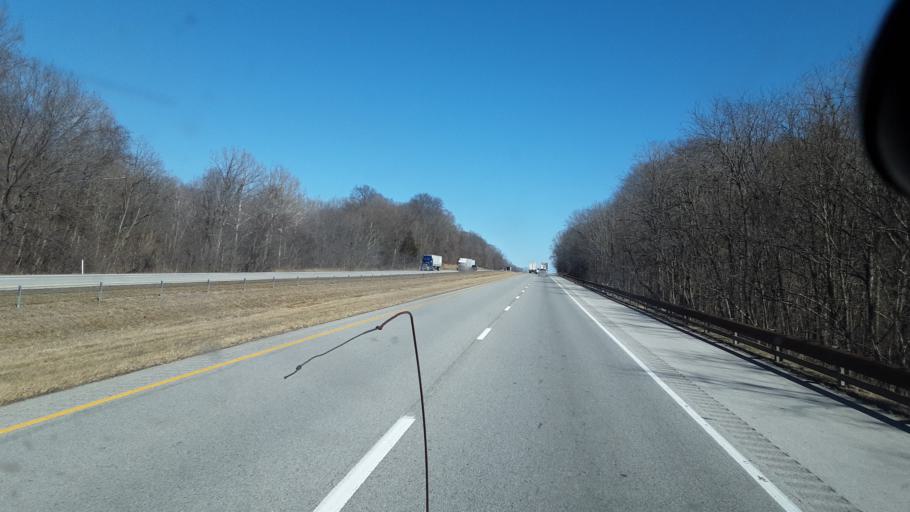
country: US
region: Indiana
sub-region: Putnam County
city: Cloverdale
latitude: 39.5080
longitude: -86.9397
